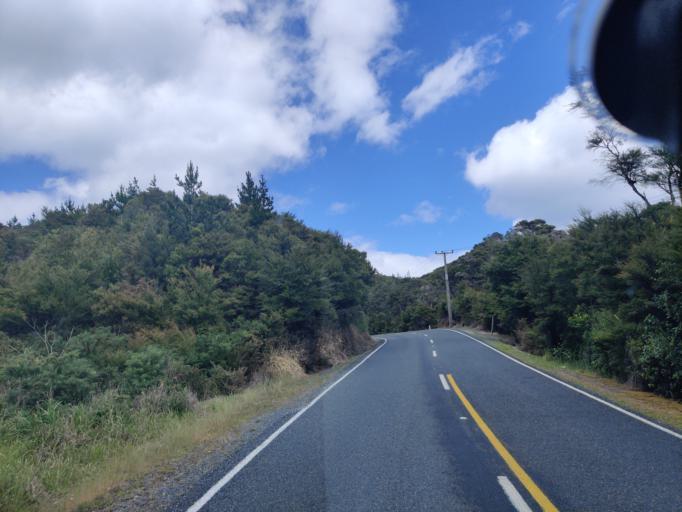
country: NZ
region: Northland
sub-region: Far North District
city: Paihia
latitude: -35.2598
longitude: 174.2237
